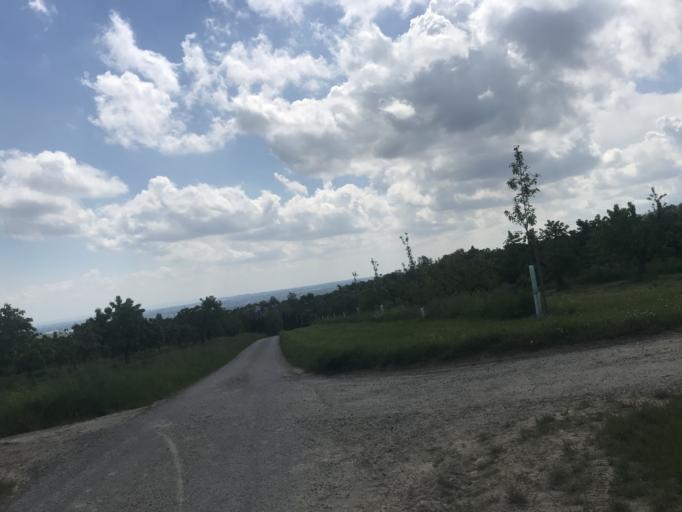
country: DE
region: Hesse
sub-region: Regierungsbezirk Darmstadt
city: Walluf
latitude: 50.0692
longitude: 8.1595
